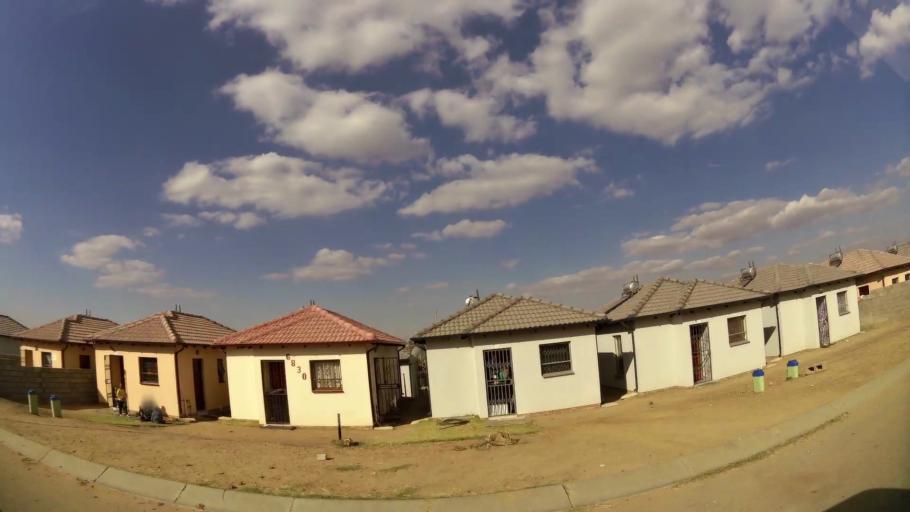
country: ZA
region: Gauteng
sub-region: Ekurhuleni Metropolitan Municipality
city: Tembisa
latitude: -25.9829
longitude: 28.1922
